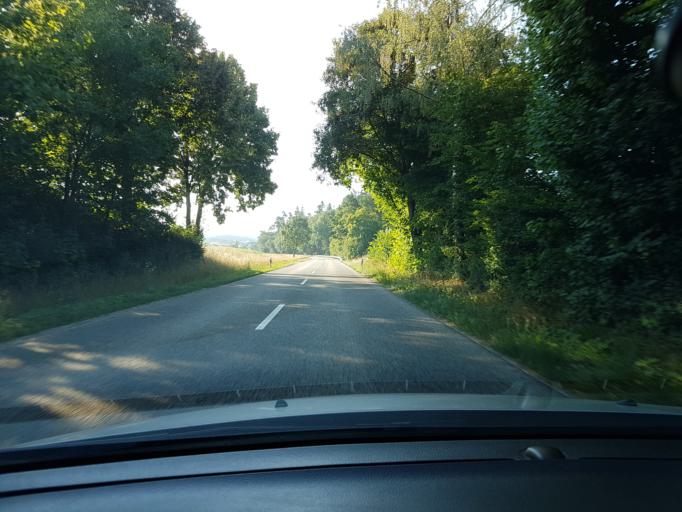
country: DE
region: Bavaria
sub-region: Lower Bavaria
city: Schalkham
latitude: 48.4977
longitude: 12.4514
